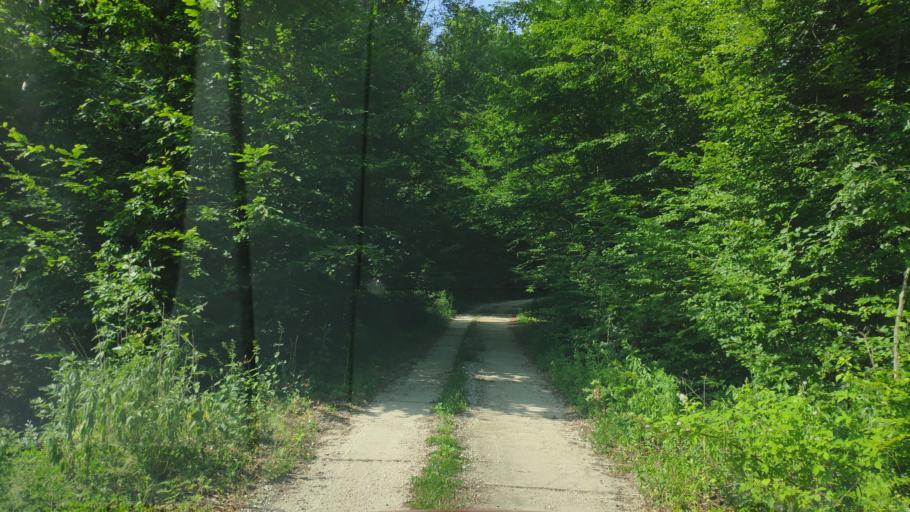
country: SK
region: Presovsky
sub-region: Okres Presov
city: Presov
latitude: 48.9733
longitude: 21.1484
